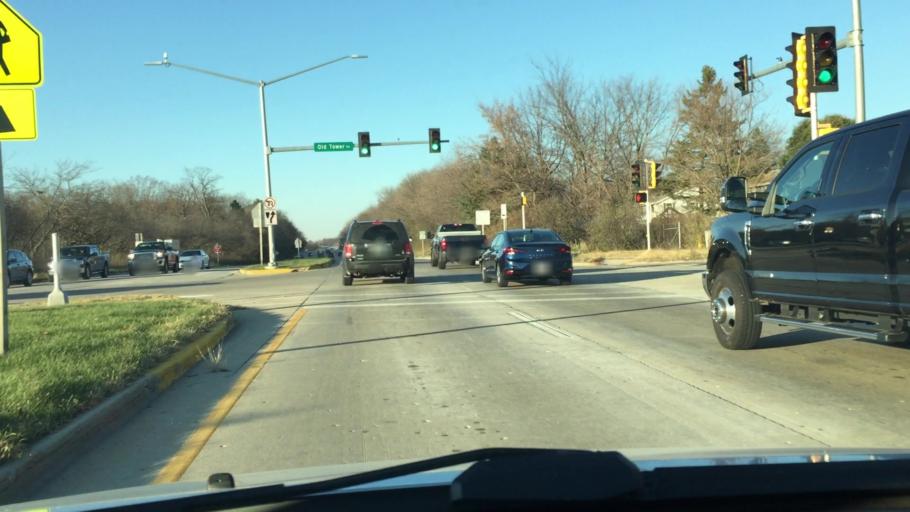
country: US
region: Wisconsin
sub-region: Waukesha County
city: Oconomowoc
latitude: 43.0968
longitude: -88.4802
